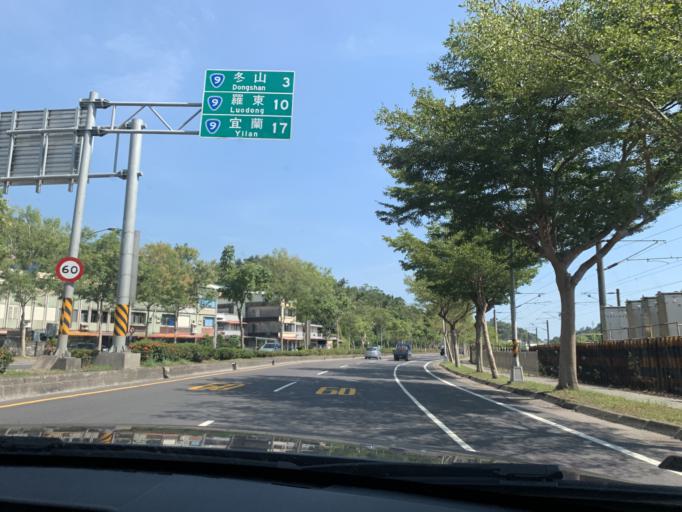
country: TW
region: Taiwan
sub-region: Yilan
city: Yilan
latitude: 24.5987
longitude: 121.8344
